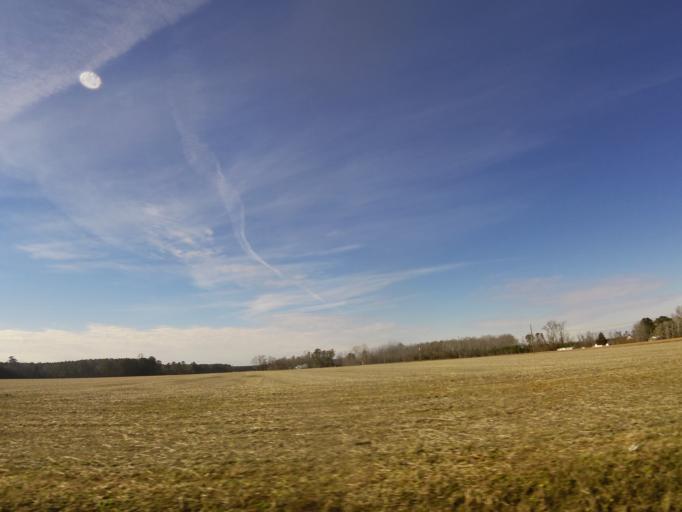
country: US
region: Virginia
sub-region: Isle of Wight County
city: Isle of Wight
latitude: 36.9012
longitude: -76.7159
